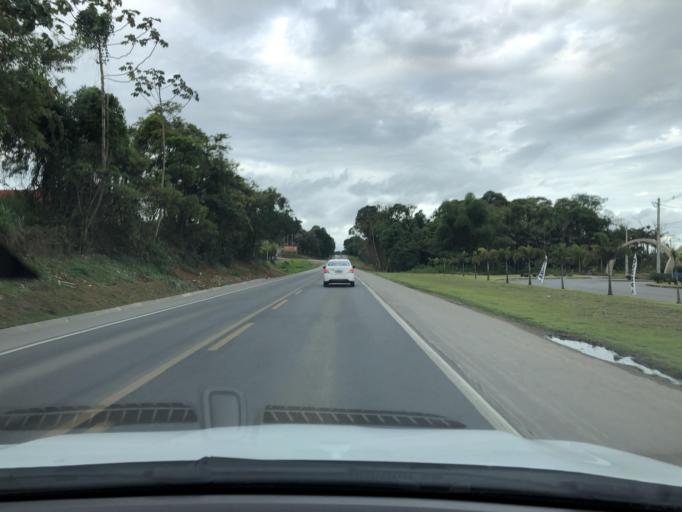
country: BR
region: Santa Catarina
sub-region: Joinville
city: Joinville
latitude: -26.4243
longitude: -48.7850
